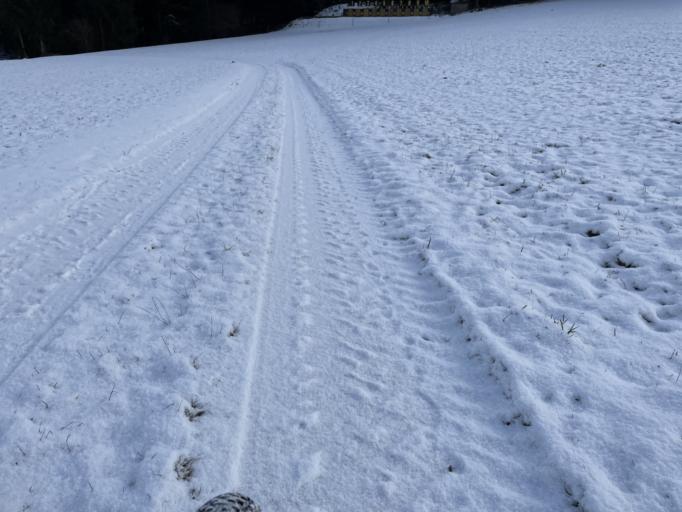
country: CH
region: Lucerne
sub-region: Entlebuch District
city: Oberdiessbach
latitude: 46.8552
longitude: 7.6098
